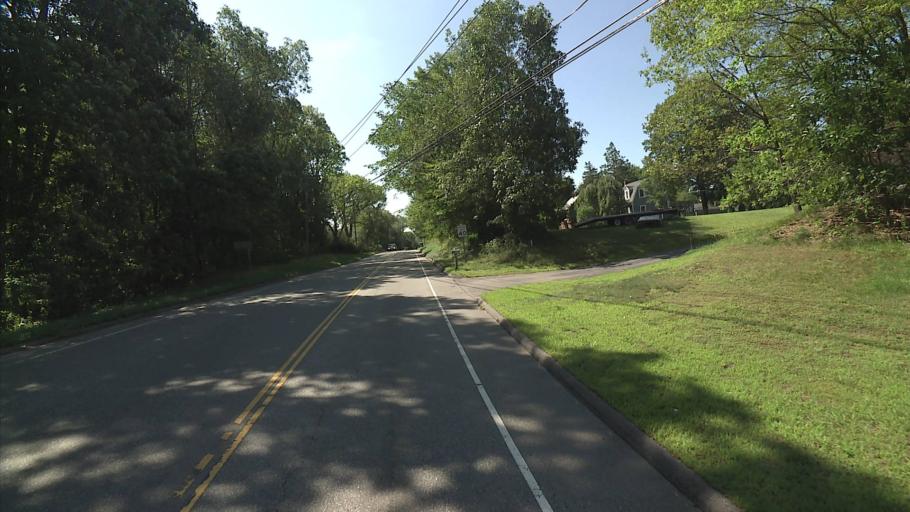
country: US
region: Connecticut
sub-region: Windham County
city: Windham
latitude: 41.7092
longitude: -72.1652
